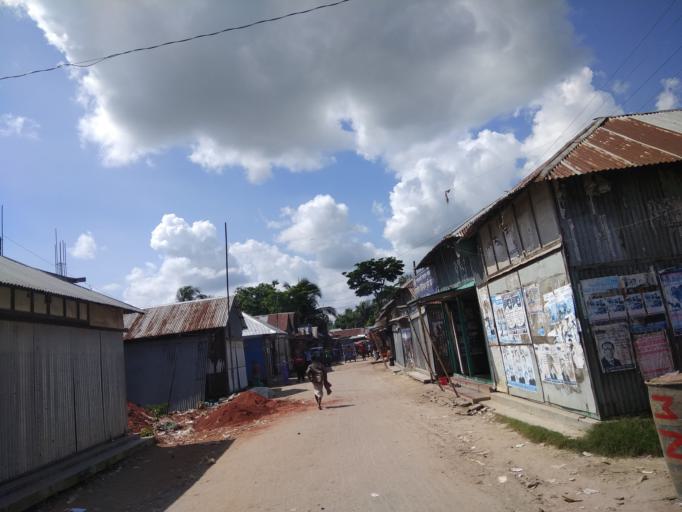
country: BD
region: Dhaka
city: Narayanganj
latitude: 23.4442
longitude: 90.4514
